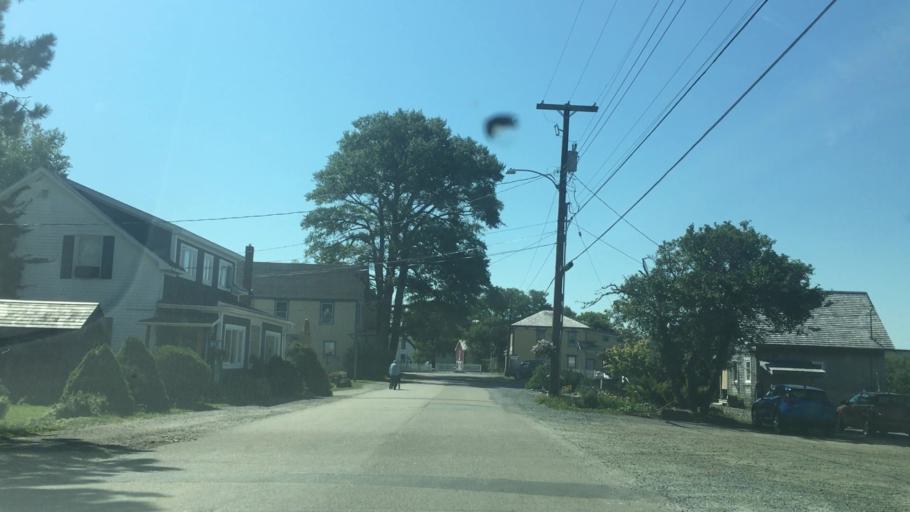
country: CA
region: Nova Scotia
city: Antigonish
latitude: 45.1418
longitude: -61.9833
